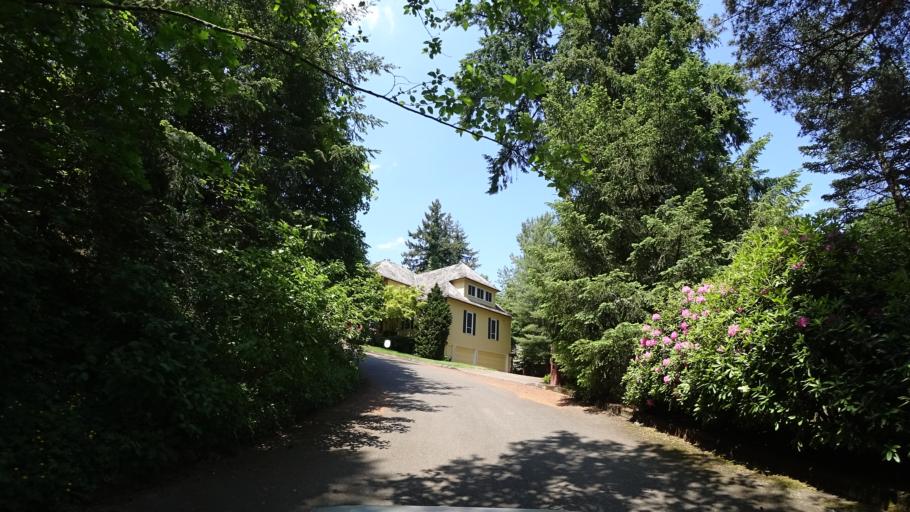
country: US
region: Oregon
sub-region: Washington County
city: Metzger
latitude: 45.4399
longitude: -122.7182
